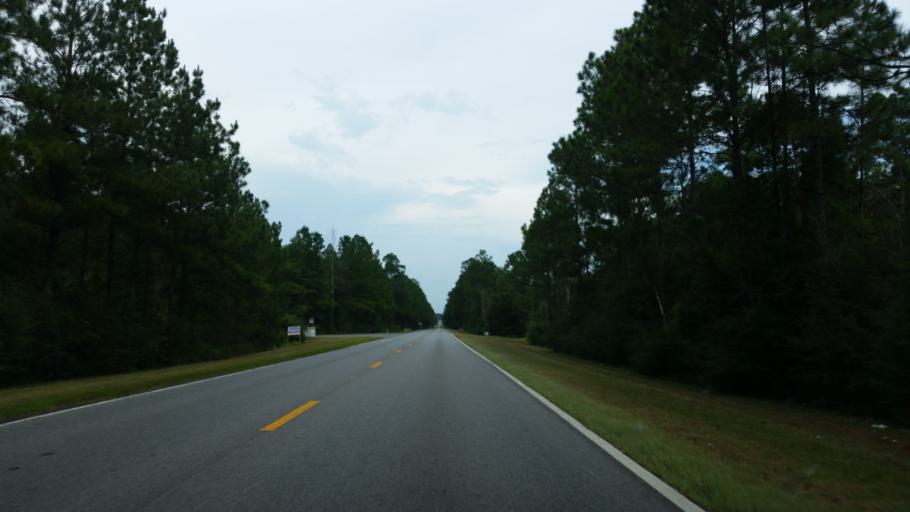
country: US
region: Florida
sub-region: Santa Rosa County
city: Wallace
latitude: 30.6731
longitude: -87.2480
